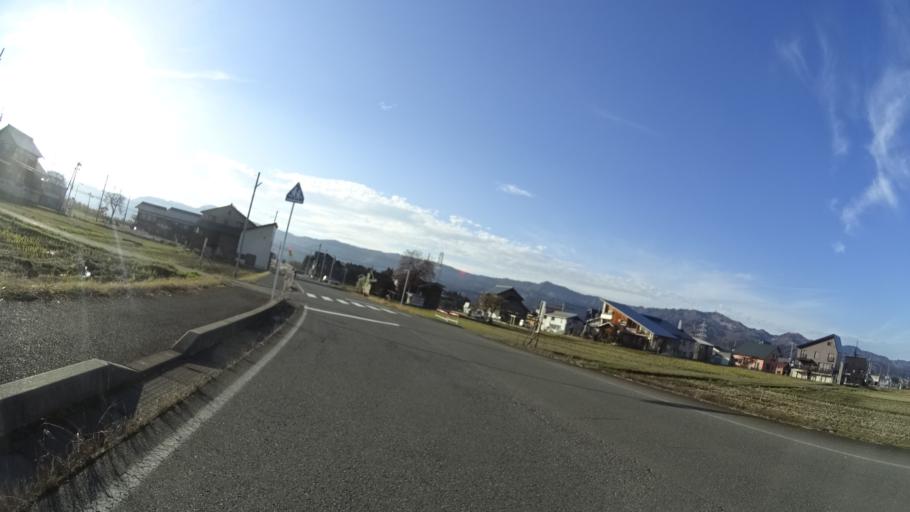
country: JP
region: Niigata
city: Shiozawa
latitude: 37.0230
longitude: 138.8660
